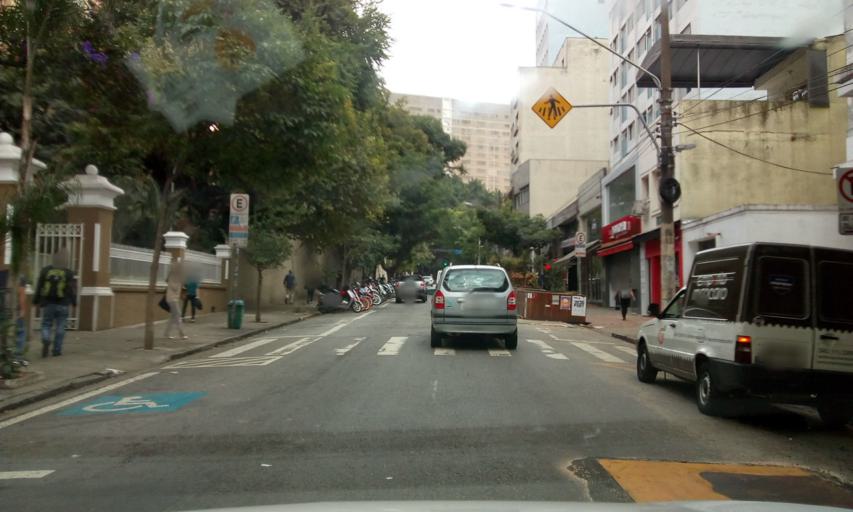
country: BR
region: Sao Paulo
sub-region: Sao Paulo
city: Sao Paulo
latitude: -23.5463
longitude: -46.6509
